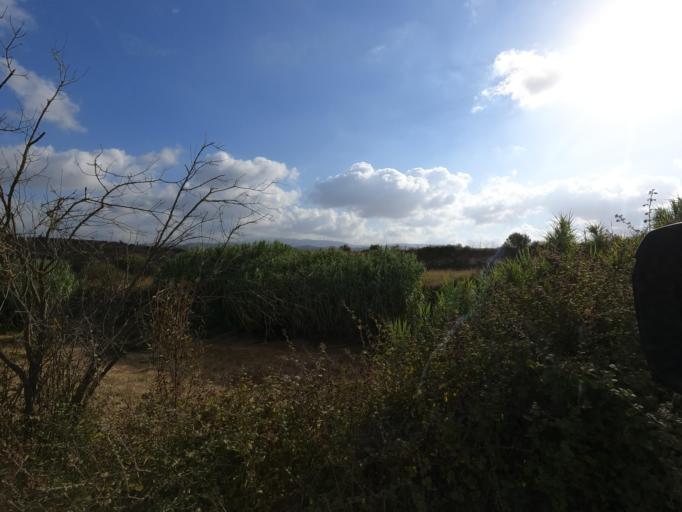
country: CY
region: Pafos
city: Mesogi
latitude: 34.8480
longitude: 32.5380
